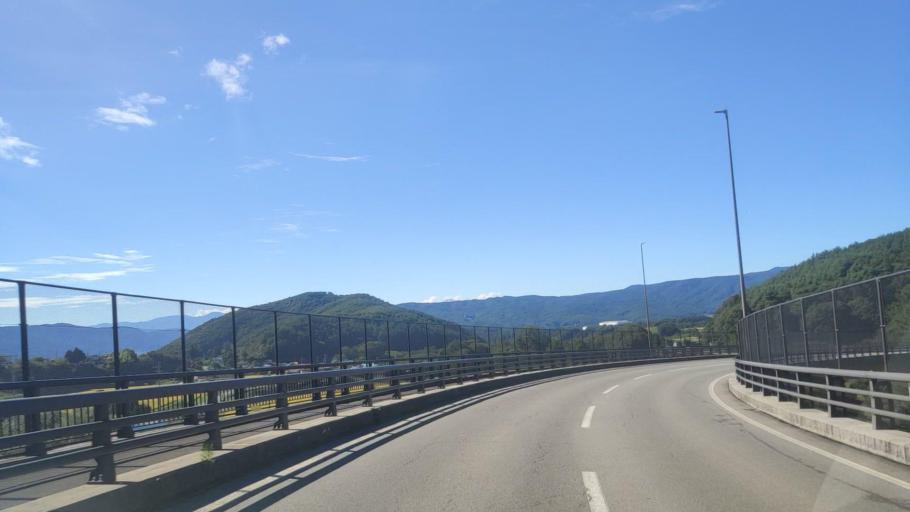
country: JP
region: Nagano
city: Chino
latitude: 35.9938
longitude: 138.2143
